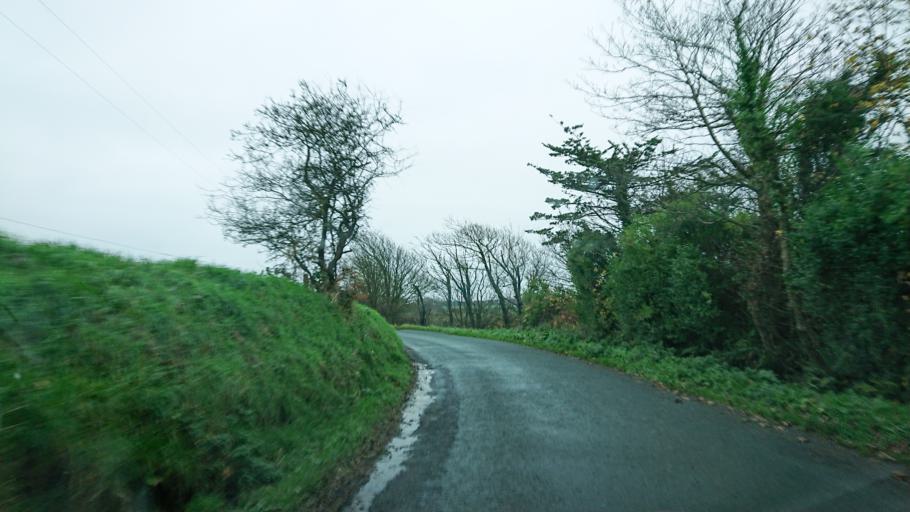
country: IE
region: Munster
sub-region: Waterford
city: Dunmore East
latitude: 52.1489
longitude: -7.0585
